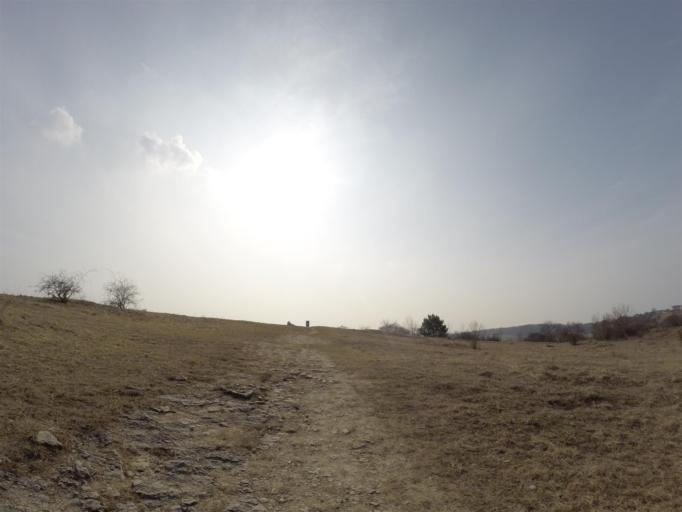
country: DE
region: Thuringia
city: Jena
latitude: 50.9454
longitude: 11.5722
